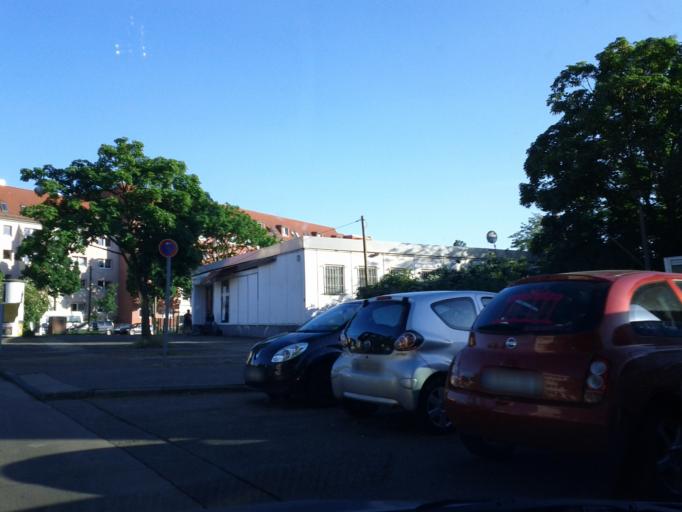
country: DE
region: Berlin
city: Kopenick Bezirk
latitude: 52.4390
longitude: 13.5642
